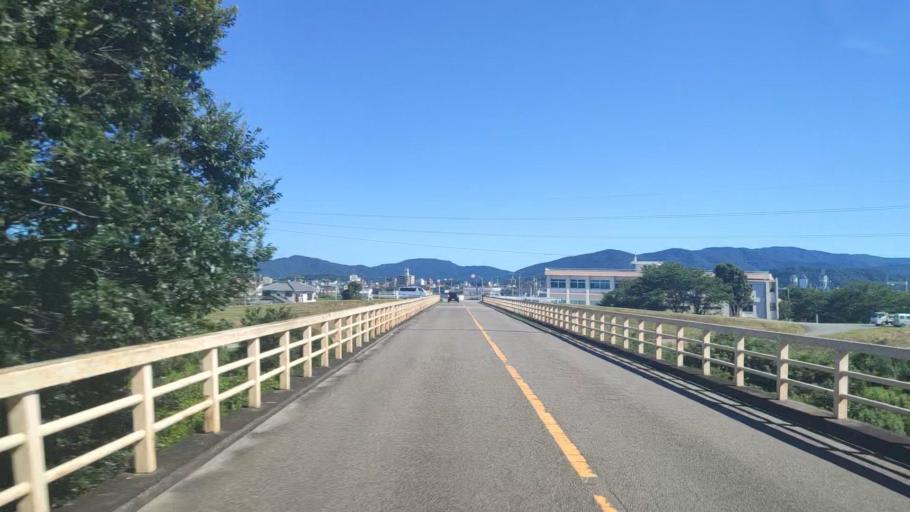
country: JP
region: Mie
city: Ise
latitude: 34.5088
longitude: 136.6940
